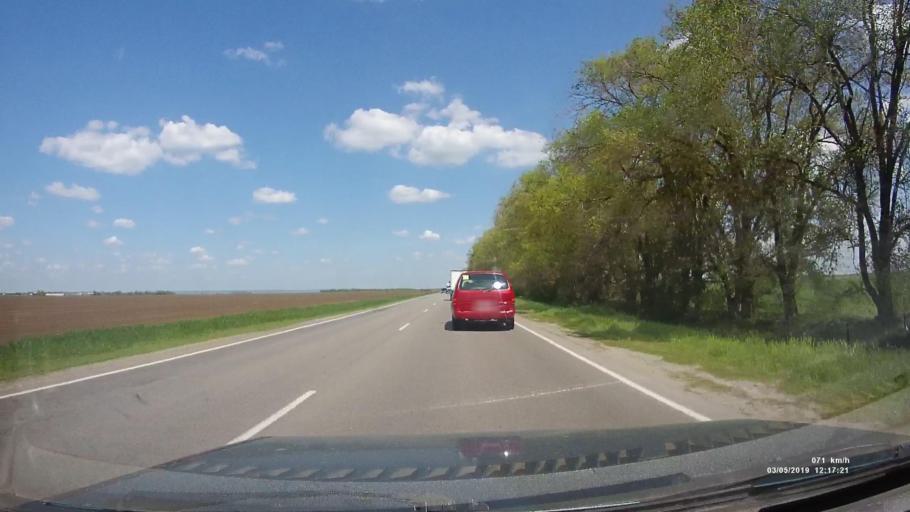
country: RU
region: Rostov
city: Melikhovskaya
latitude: 47.3816
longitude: 40.5915
